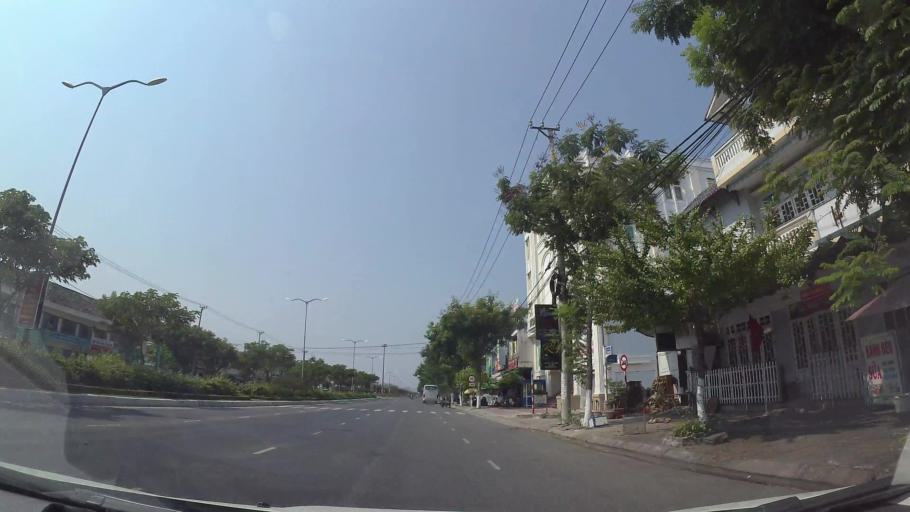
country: VN
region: Da Nang
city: Ngu Hanh Son
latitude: 16.0085
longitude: 108.2582
